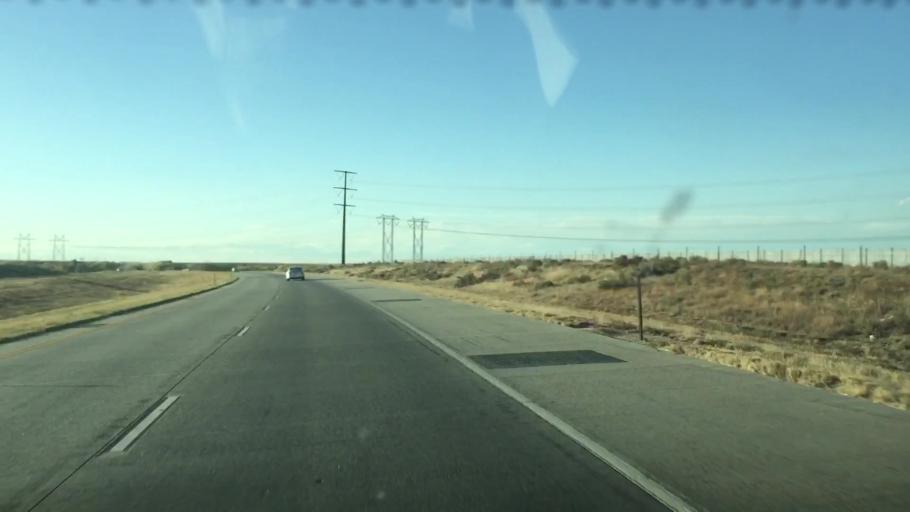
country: US
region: Colorado
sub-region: Arapahoe County
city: Byers
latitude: 39.6640
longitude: -104.0857
